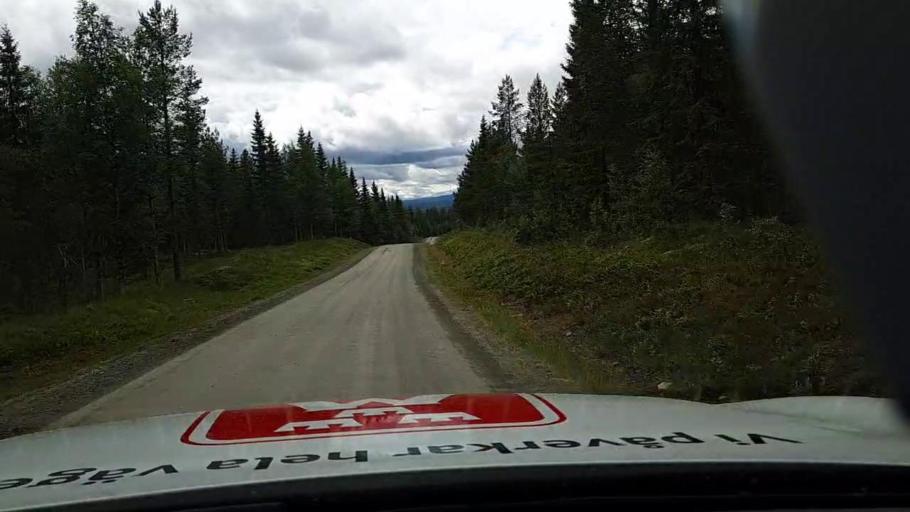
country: SE
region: Jaemtland
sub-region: Are Kommun
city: Jarpen
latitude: 62.8307
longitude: 13.8219
